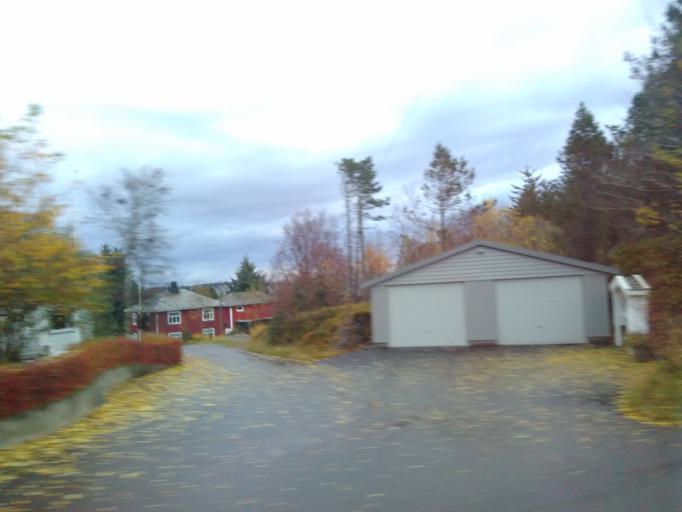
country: NO
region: Sor-Trondelag
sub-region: Froya
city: Sistranda
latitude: 63.7469
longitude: 8.8357
